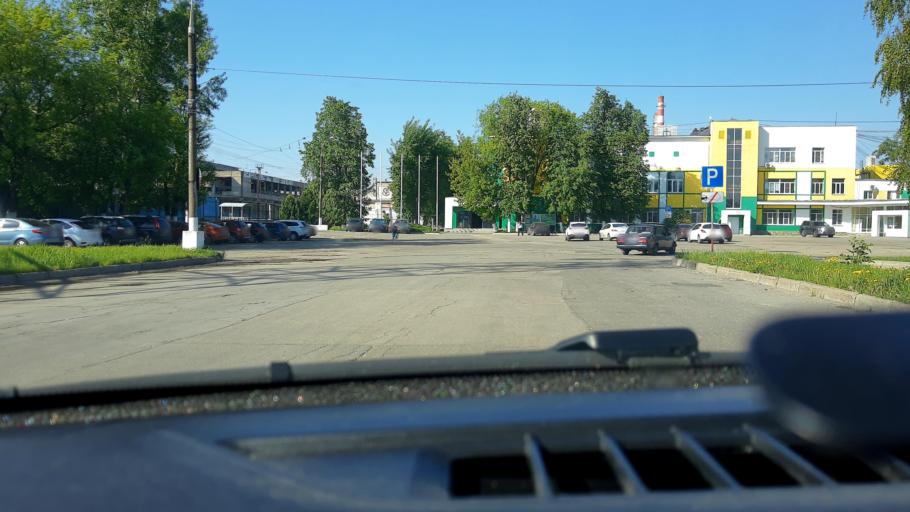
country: RU
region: Nizjnij Novgorod
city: Nizhniy Novgorod
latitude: 56.3116
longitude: 43.9172
